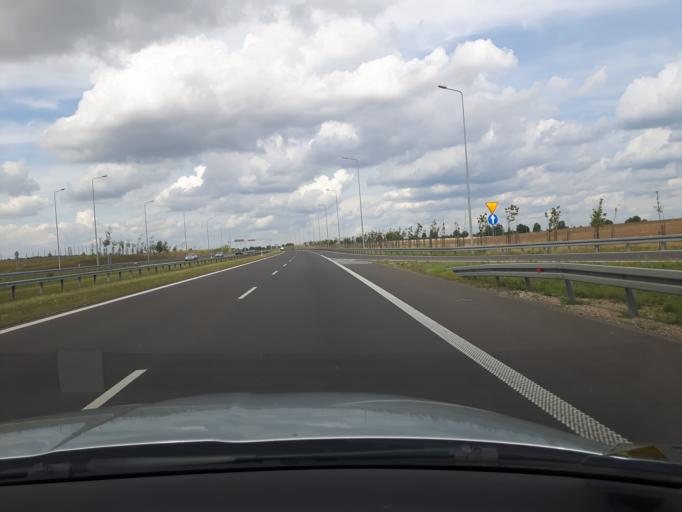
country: PL
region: Warmian-Masurian Voivodeship
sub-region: Powiat nidzicki
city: Nidzica
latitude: 53.2776
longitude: 20.4375
